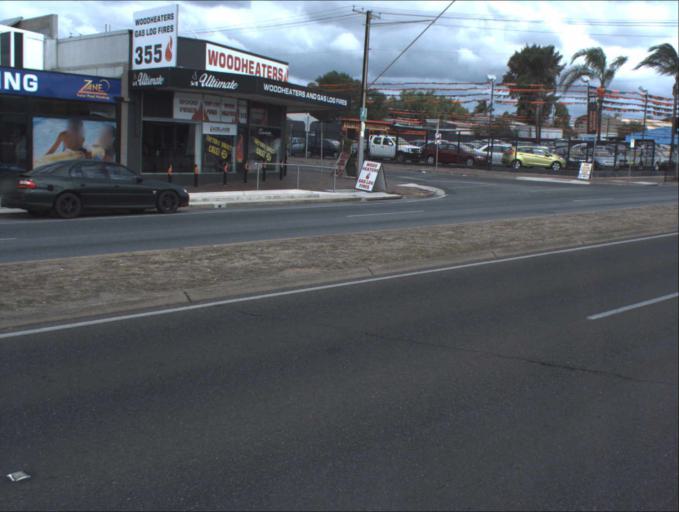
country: AU
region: South Australia
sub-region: Port Adelaide Enfield
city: Blair Athol
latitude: -34.8645
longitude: 138.6012
